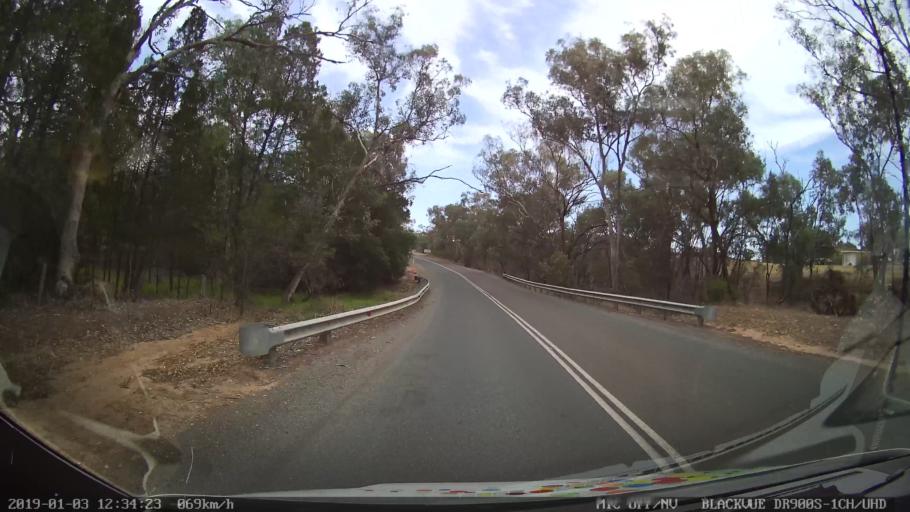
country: AU
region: New South Wales
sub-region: Weddin
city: Grenfell
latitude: -33.8771
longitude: 148.1666
